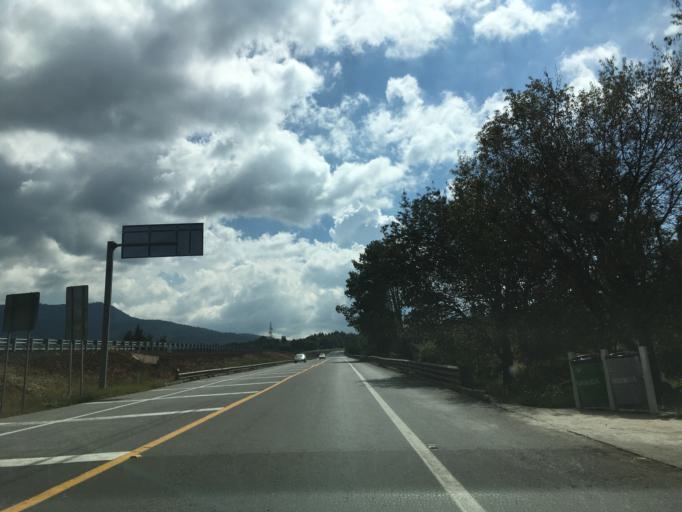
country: MX
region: Michoacan
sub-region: Patzcuaro
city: Colonia Vista Bella (Lomas del Peaje)
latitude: 19.5159
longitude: -101.5735
